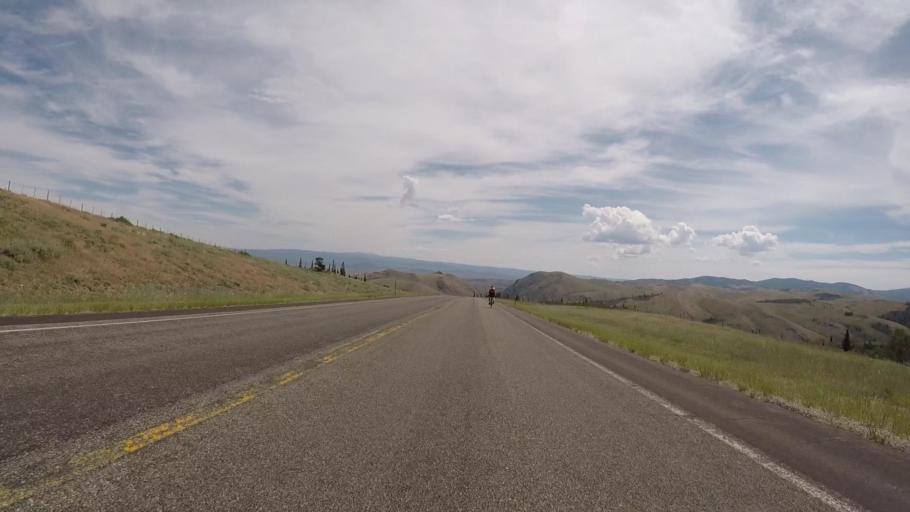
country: US
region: Wyoming
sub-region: Carbon County
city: Saratoga
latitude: 41.1818
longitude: -106.8695
